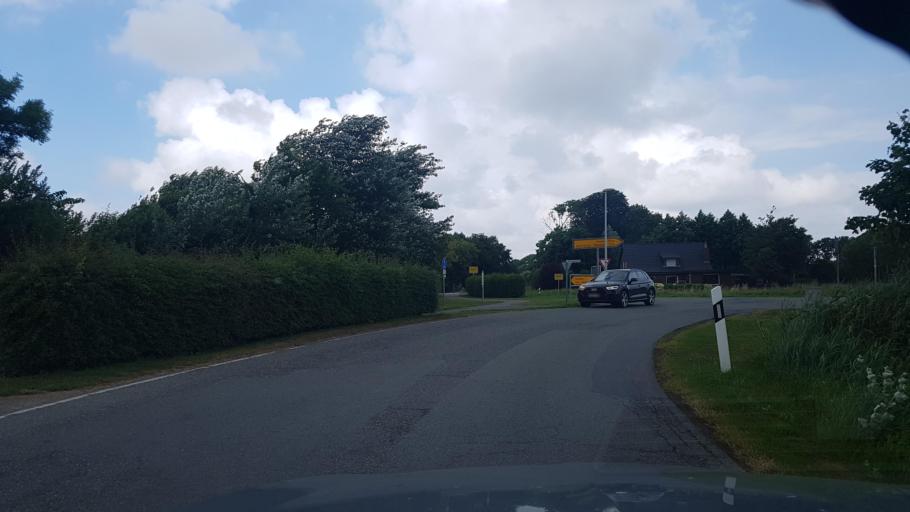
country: DE
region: Schleswig-Holstein
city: Elisabeth-Sophien-Koog
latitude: 54.4880
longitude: 8.8488
